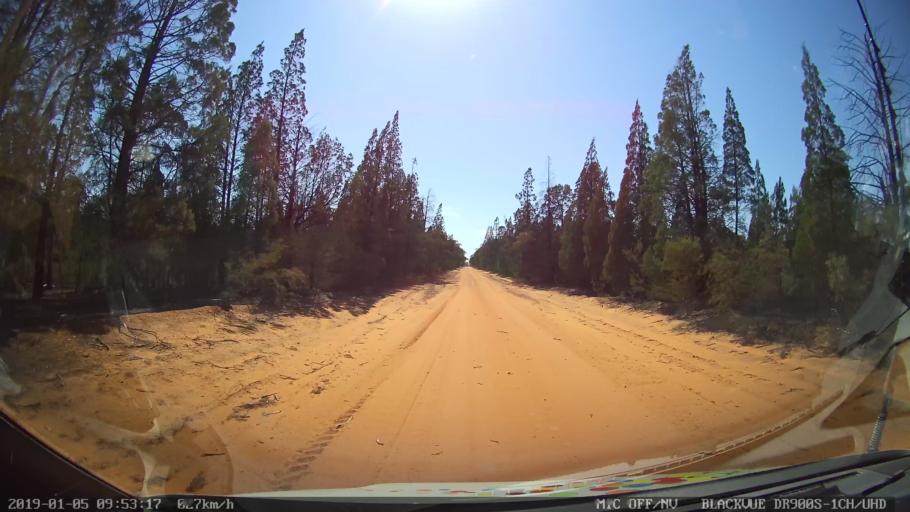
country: AU
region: New South Wales
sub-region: Gilgandra
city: Gilgandra
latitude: -31.6621
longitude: 148.7723
